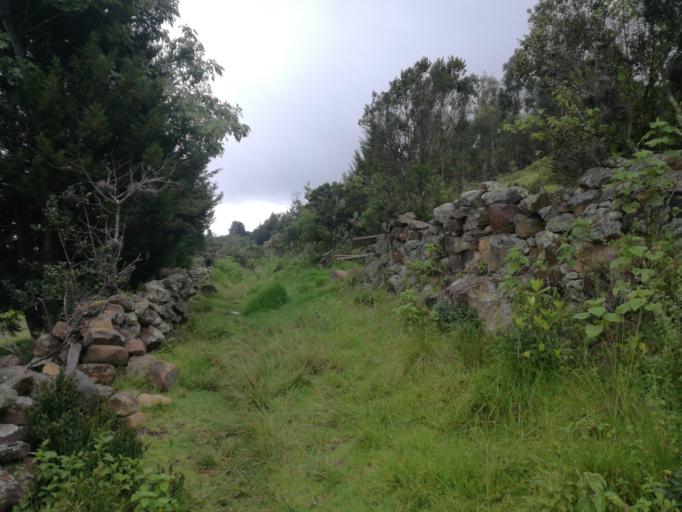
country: CO
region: Boyaca
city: Socha Viejo
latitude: 6.0045
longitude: -72.6823
